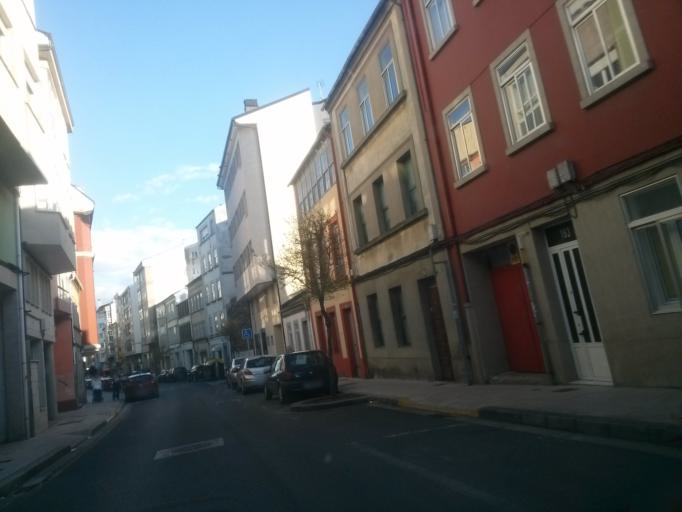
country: ES
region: Galicia
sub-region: Provincia de Lugo
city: Lugo
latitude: 43.0204
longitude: -7.5680
